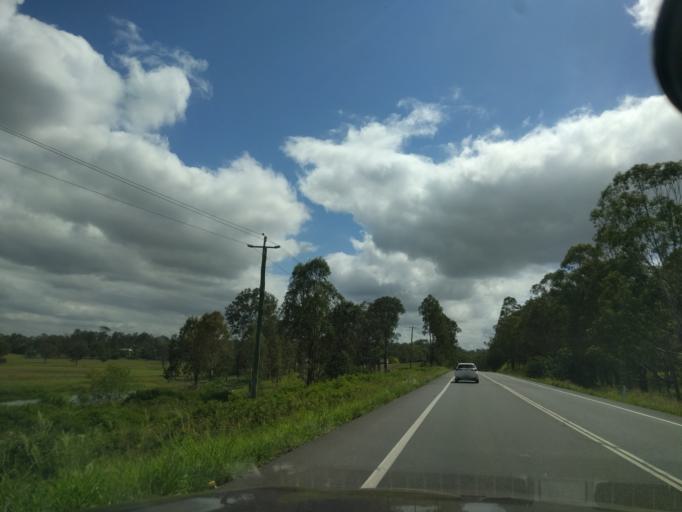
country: AU
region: Queensland
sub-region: Logan
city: Cedar Vale
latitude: -27.8870
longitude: 152.9776
